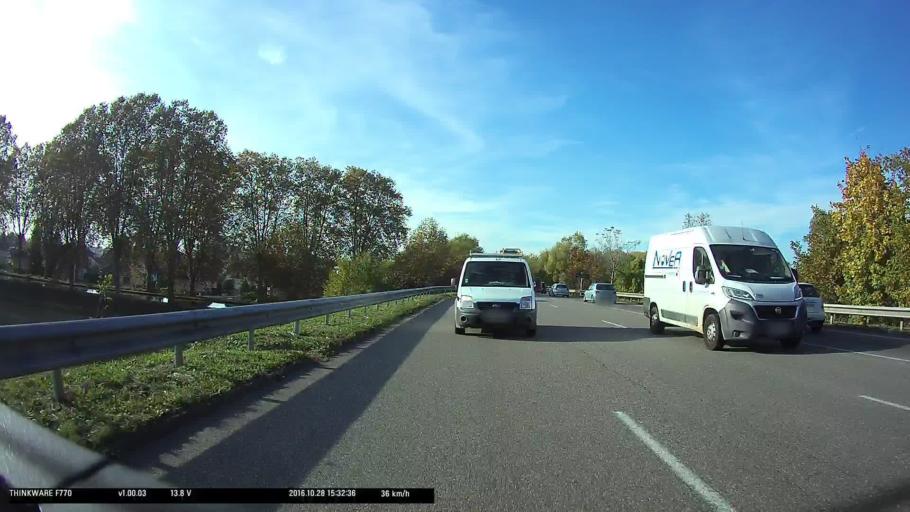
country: FR
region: Alsace
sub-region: Departement du Bas-Rhin
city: Ostwald
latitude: 48.5442
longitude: 7.7330
